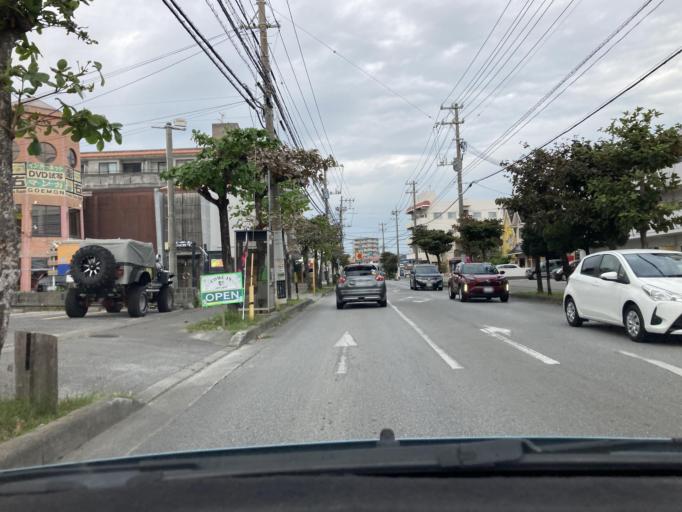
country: JP
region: Okinawa
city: Chatan
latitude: 26.3074
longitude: 127.7612
